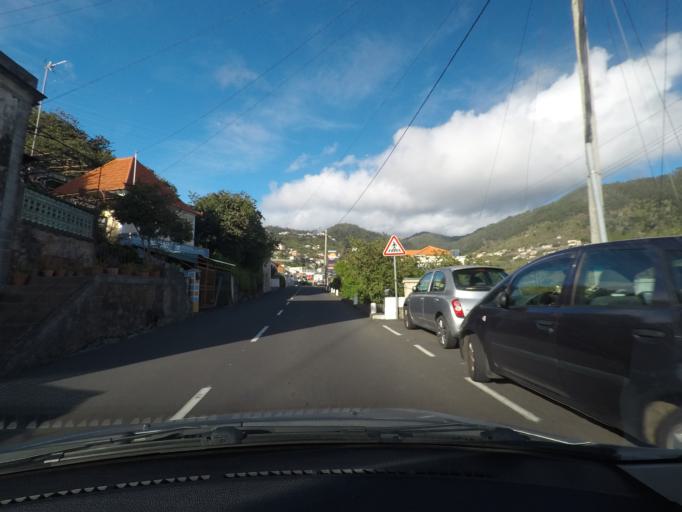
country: PT
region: Madeira
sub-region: Ribeira Brava
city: Campanario
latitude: 32.6700
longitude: -17.0304
